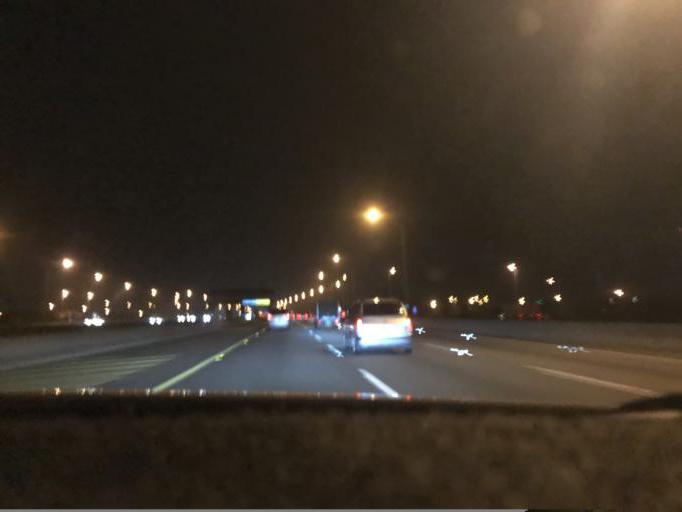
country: TW
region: Taiwan
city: Fengyuan
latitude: 24.3776
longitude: 120.6655
